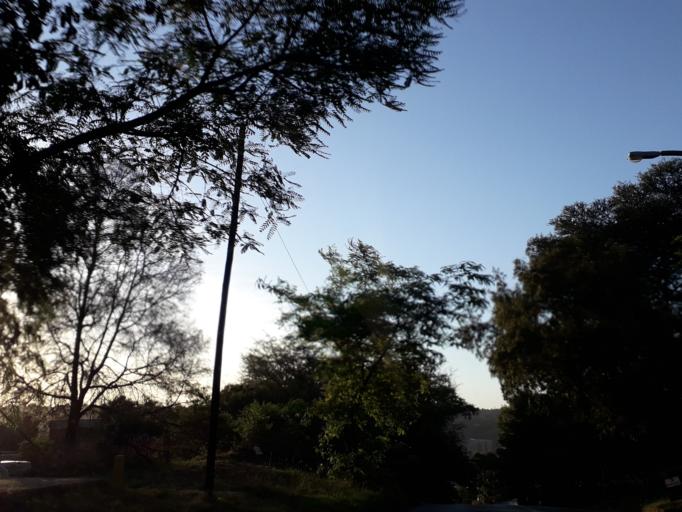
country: ZA
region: Gauteng
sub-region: City of Johannesburg Metropolitan Municipality
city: Roodepoort
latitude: -26.1551
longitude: 27.9313
